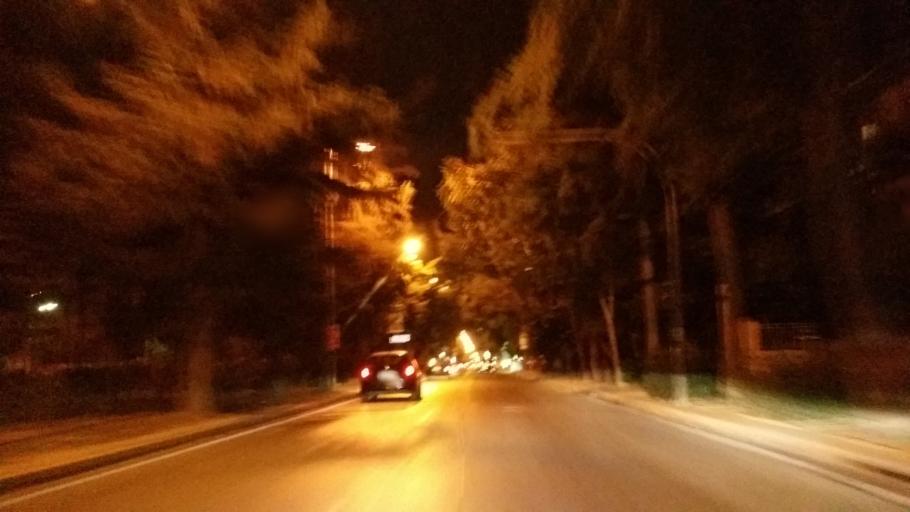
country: GR
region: Attica
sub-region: Nomarchia Athinas
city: Filothei
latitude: 38.0255
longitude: 23.7870
